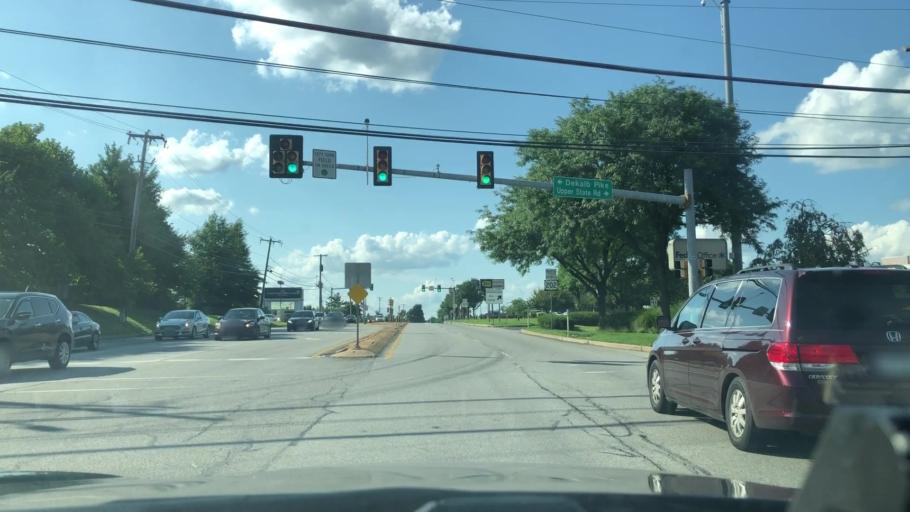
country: US
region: Pennsylvania
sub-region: Montgomery County
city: Montgomeryville
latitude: 40.2352
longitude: -75.2399
